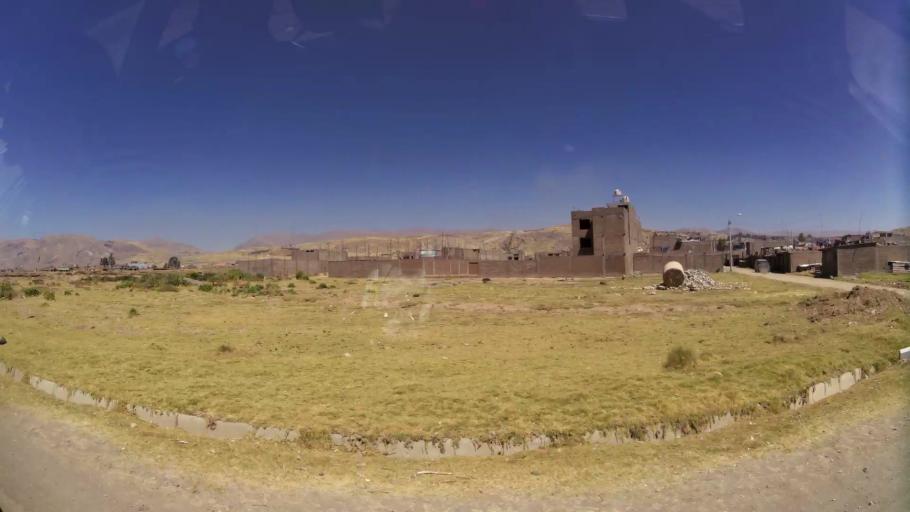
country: PE
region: Junin
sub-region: Provincia de Jauja
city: Jauja
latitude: -11.7744
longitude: -75.4883
